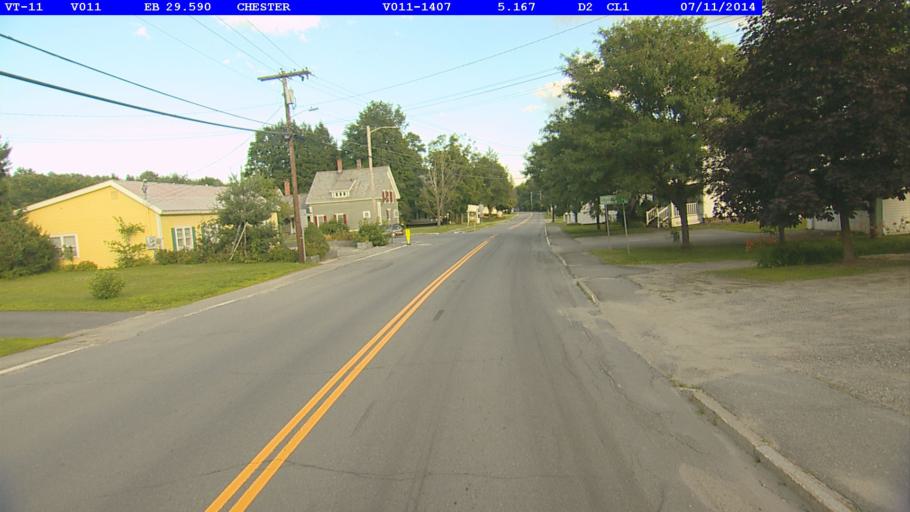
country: US
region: Vermont
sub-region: Windsor County
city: Chester
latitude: 43.2624
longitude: -72.5939
